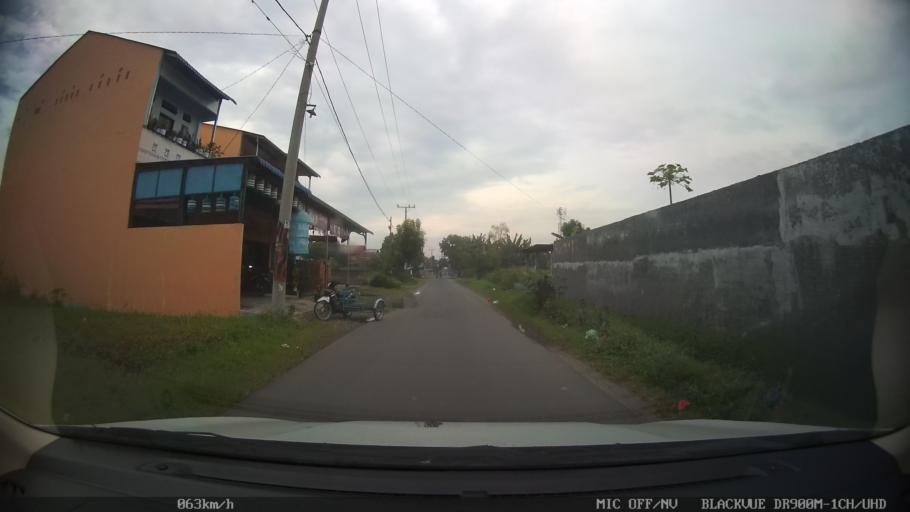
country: ID
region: North Sumatra
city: Sunggal
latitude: 3.6142
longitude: 98.5946
